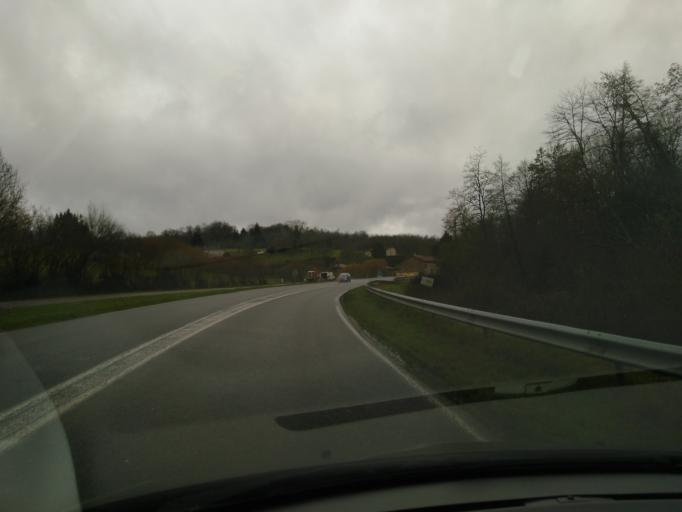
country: FR
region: Limousin
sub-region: Departement de la Haute-Vienne
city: Le Vigen
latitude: 45.7408
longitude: 1.2842
